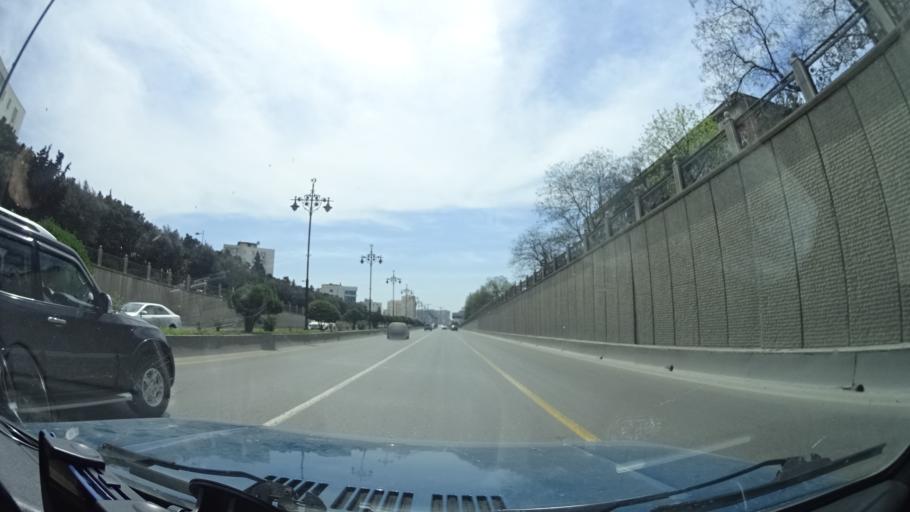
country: AZ
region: Baki
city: Bilajari
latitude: 40.4089
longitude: 49.8048
